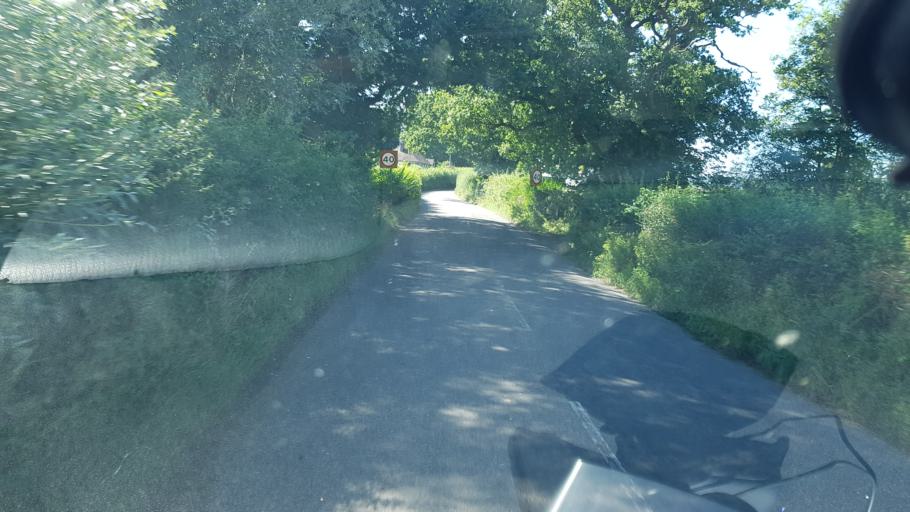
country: GB
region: England
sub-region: Kent
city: Edenbridge
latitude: 51.2221
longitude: 0.0852
